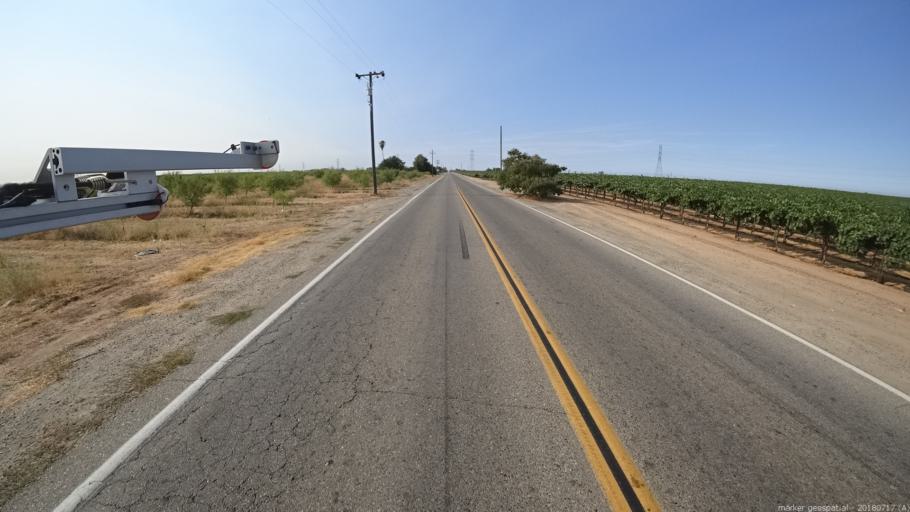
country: US
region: California
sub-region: Madera County
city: Madera Acres
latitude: 37.0471
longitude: -120.1107
